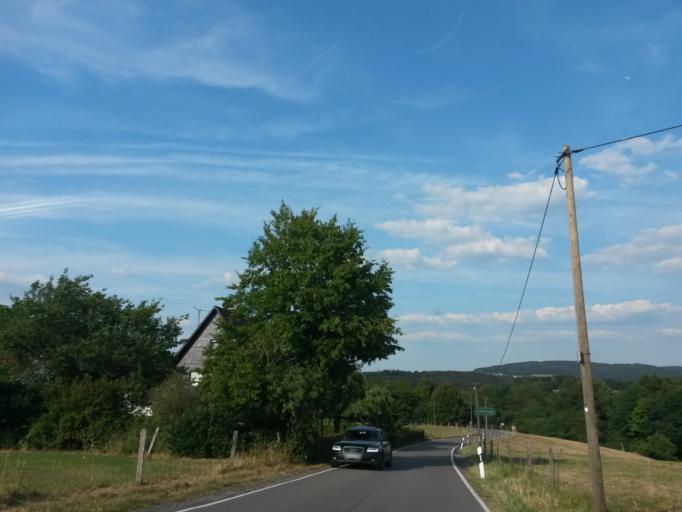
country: DE
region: North Rhine-Westphalia
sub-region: Regierungsbezirk Koln
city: Overath
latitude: 50.9449
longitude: 7.3251
